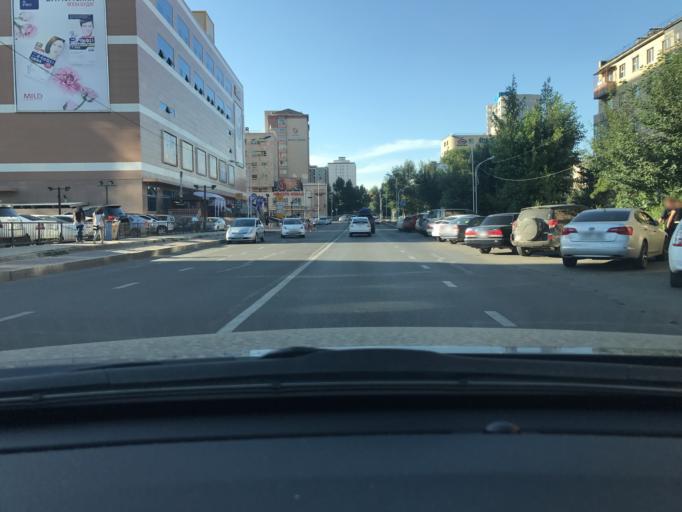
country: MN
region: Ulaanbaatar
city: Ulaanbaatar
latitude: 47.9222
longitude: 106.9350
